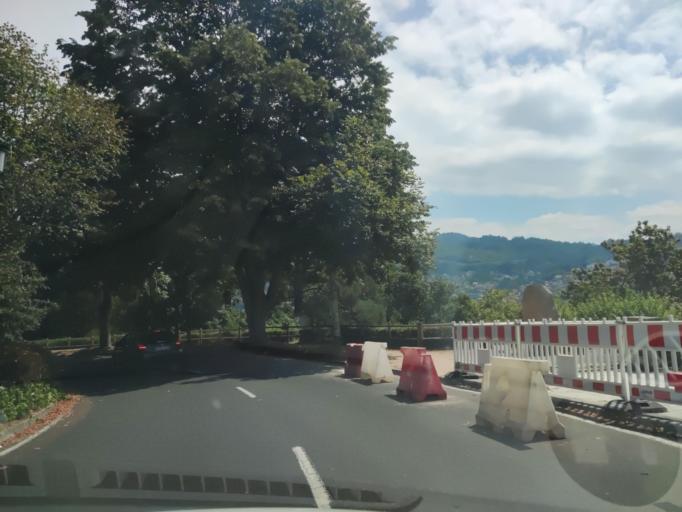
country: ES
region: Galicia
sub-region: Provincia de Pontevedra
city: Vigo
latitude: 42.2553
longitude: -8.7019
